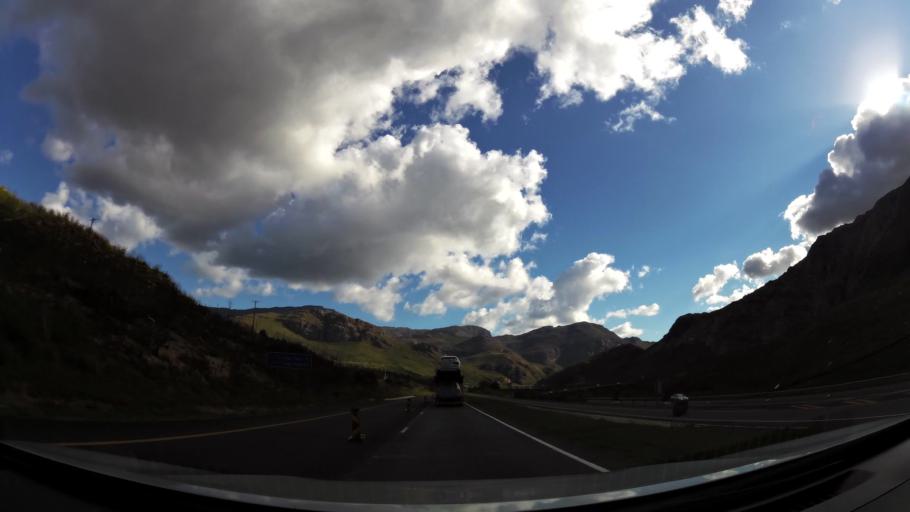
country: ZA
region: Western Cape
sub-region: Cape Winelands District Municipality
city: Paarl
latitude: -33.7262
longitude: 19.1413
